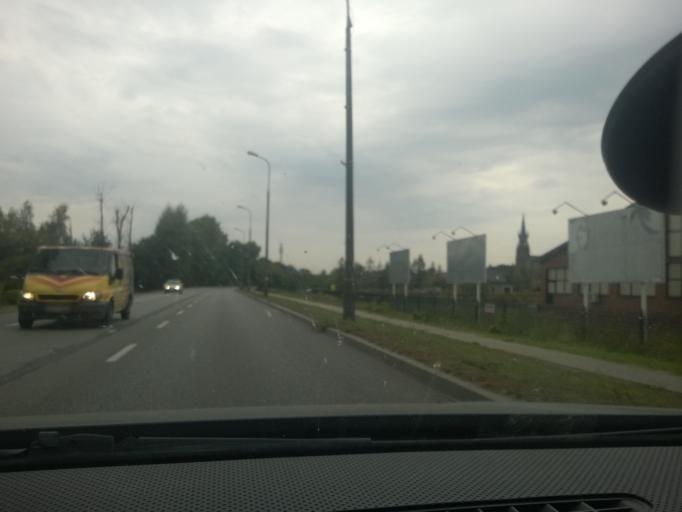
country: PL
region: Masovian Voivodeship
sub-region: Powiat pruszkowski
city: Pruszkow
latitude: 52.1771
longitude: 20.7903
